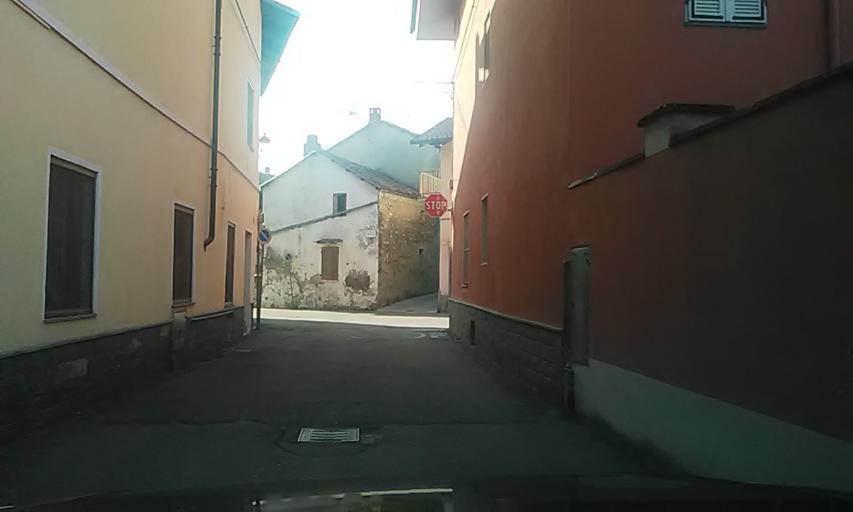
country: IT
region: Piedmont
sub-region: Provincia di Vercelli
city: Alice Castello
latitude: 45.3644
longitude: 8.0764
